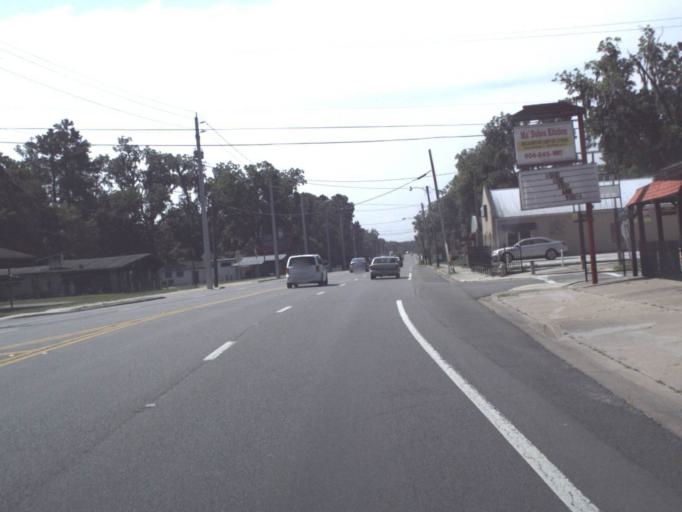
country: US
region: Florida
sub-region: Nassau County
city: Hilliard
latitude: 30.6901
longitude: -81.9172
